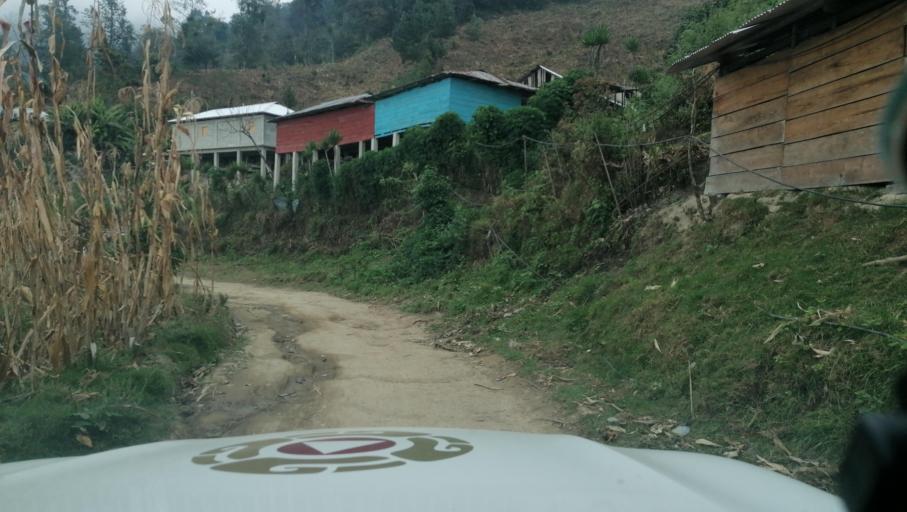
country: GT
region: San Marcos
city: Tacana
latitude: 15.2039
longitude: -92.1682
